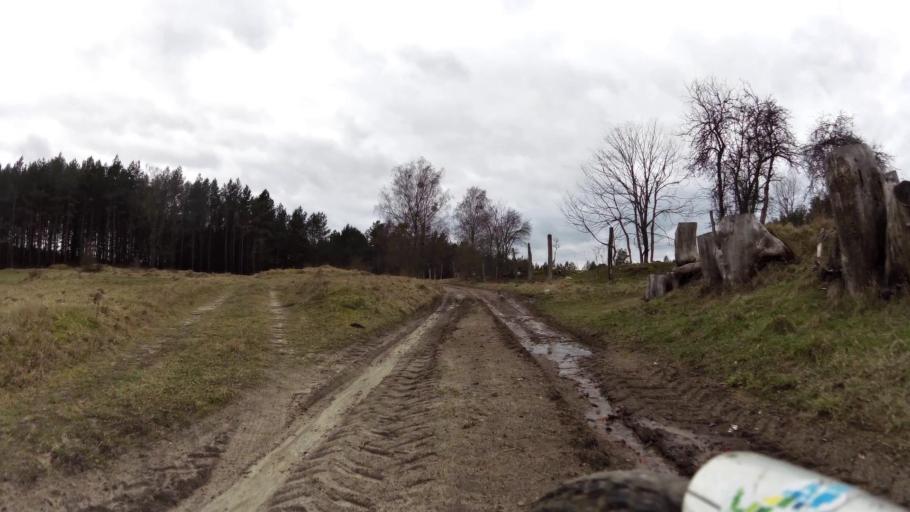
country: PL
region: Pomeranian Voivodeship
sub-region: Powiat bytowski
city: Trzebielino
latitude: 54.1386
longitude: 17.1478
